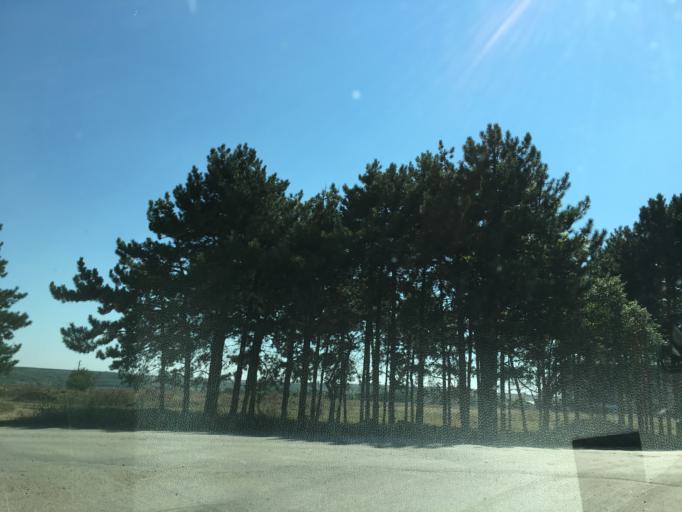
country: BG
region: Pleven
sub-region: Obshtina Knezha
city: Knezha
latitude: 43.5141
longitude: 24.0955
